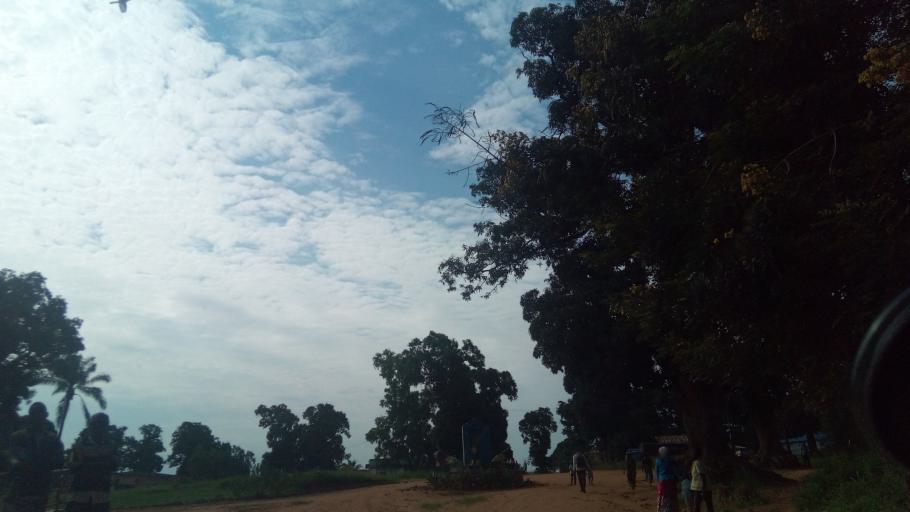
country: CD
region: Kasai-Oriental
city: Kabinda
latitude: -6.1333
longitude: 24.4849
